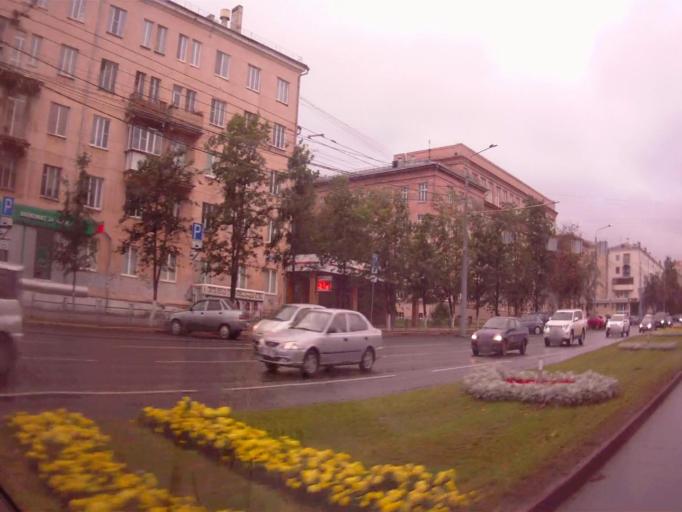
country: RU
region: Chelyabinsk
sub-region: Gorod Chelyabinsk
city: Chelyabinsk
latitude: 55.1600
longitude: 61.3857
